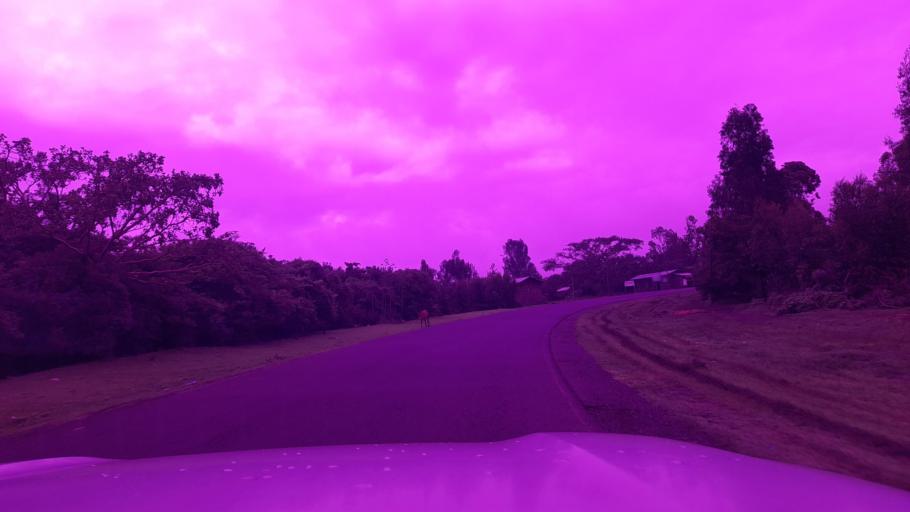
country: ET
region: Oromiya
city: Waliso
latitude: 8.2806
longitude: 37.6861
